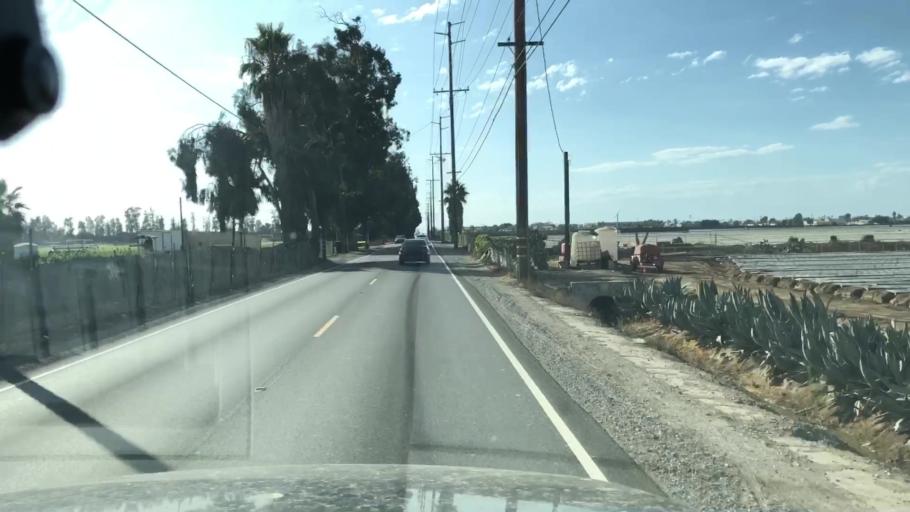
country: US
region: California
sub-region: Ventura County
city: Oxnard
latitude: 34.1898
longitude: -119.1505
